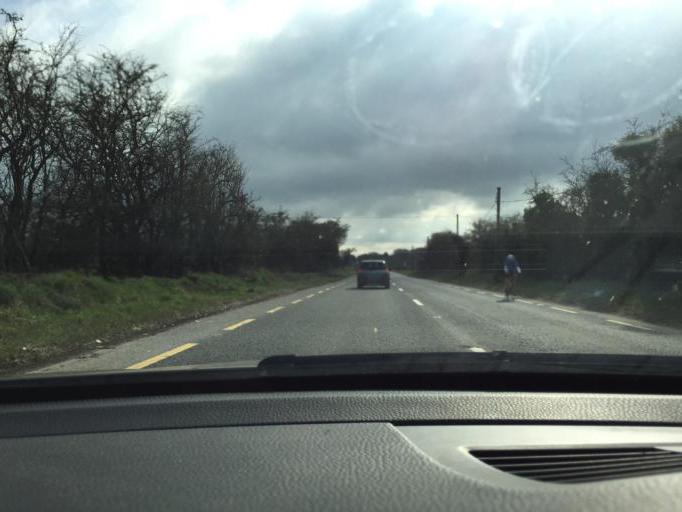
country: IE
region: Leinster
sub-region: South Dublin
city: Saggart
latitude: 53.2289
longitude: -6.4619
